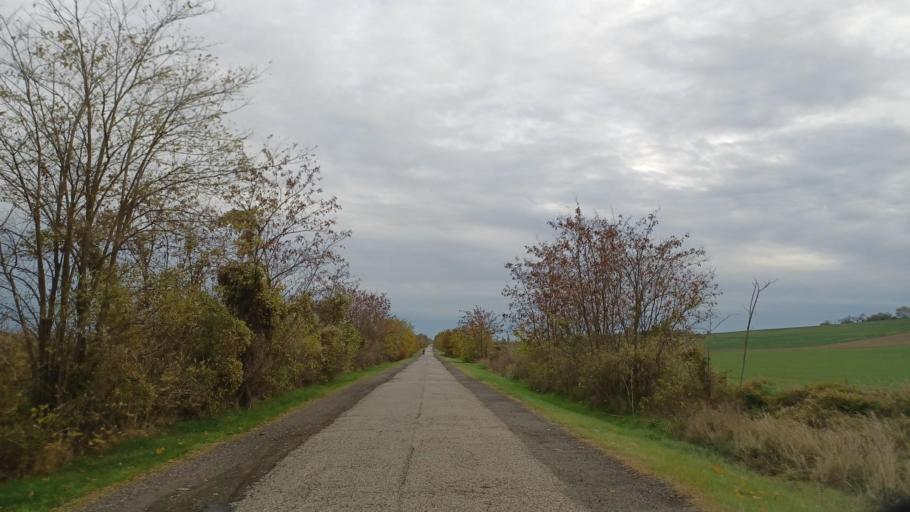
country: HU
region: Tolna
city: Simontornya
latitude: 46.6969
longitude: 18.5893
